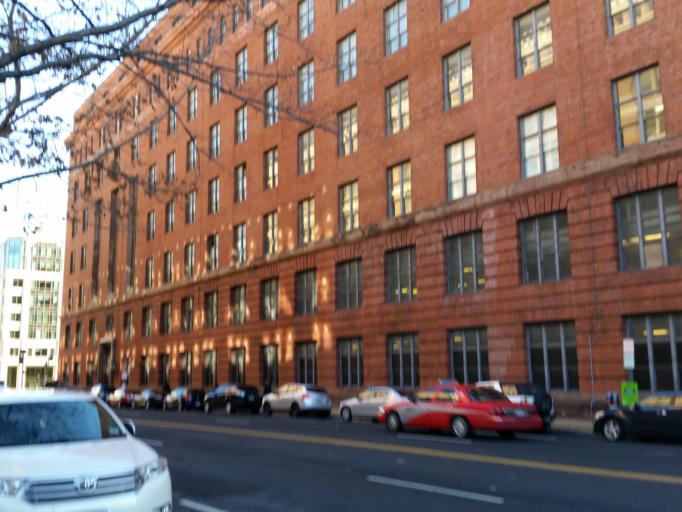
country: US
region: Washington, D.C.
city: Washington, D.C.
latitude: 38.9003
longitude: -77.0105
